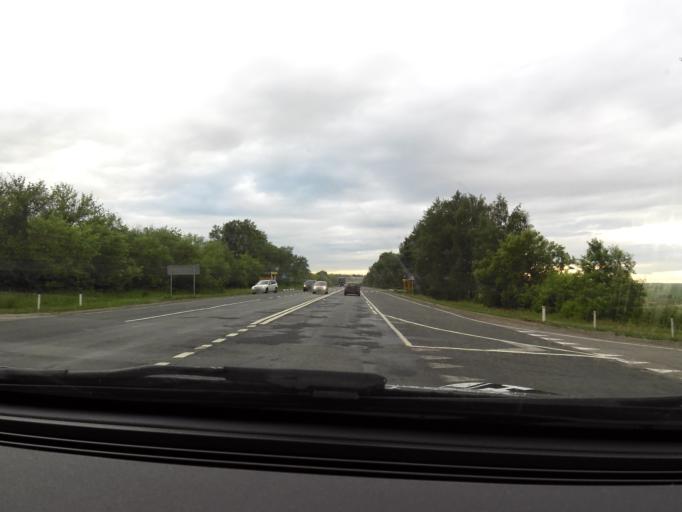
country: RU
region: Chuvashia
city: Yantikovo
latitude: 55.7898
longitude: 47.6961
